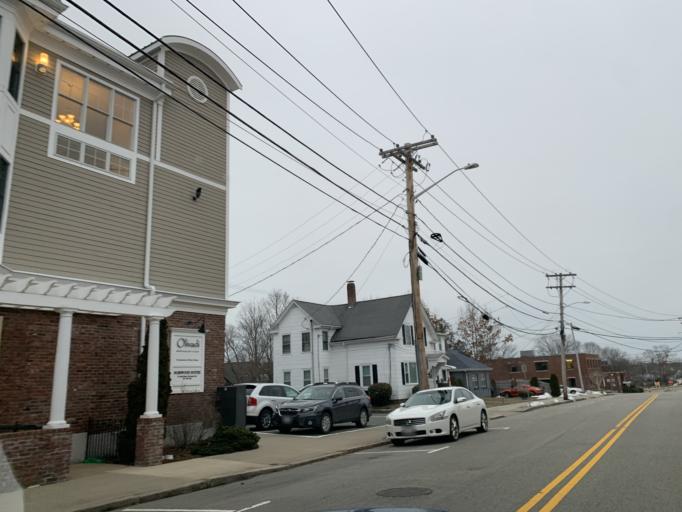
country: US
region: Massachusetts
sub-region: Norfolk County
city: Norwood
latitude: 42.1906
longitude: -71.2014
